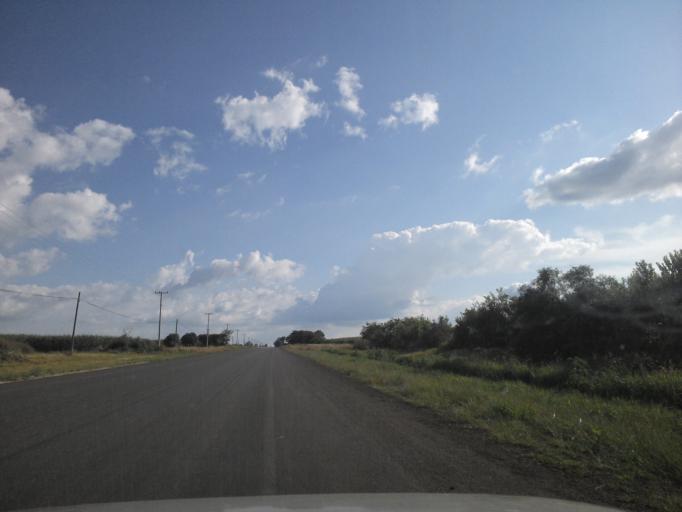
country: MX
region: Jalisco
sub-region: Atotonilco el Alto
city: Ojo de Agua de Moran
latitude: 20.5990
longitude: -102.4931
